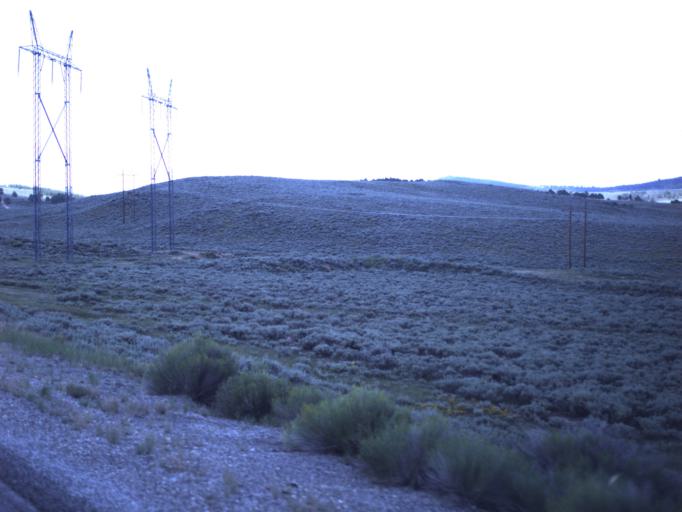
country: US
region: Utah
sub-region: Carbon County
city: Helper
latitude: 39.8391
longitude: -111.1293
